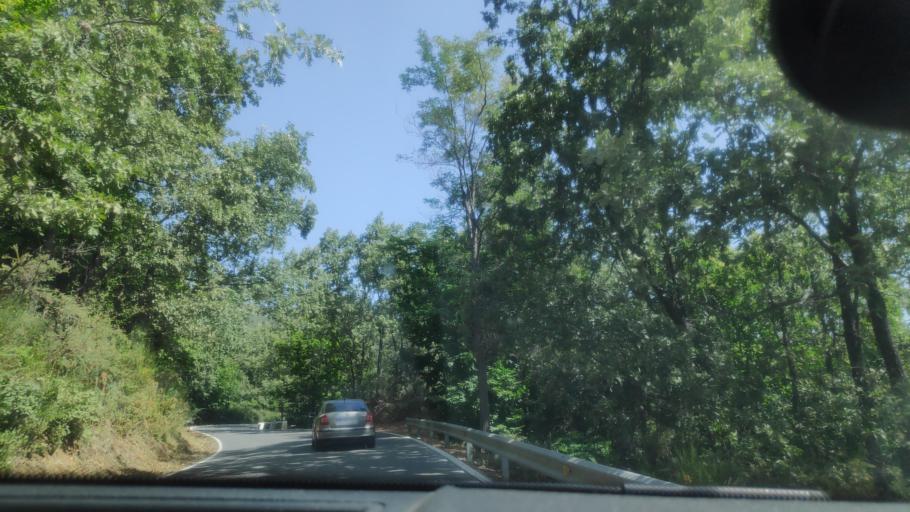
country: ES
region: Andalusia
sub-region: Provincia de Granada
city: Busquistar
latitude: 36.9471
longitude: -3.2852
